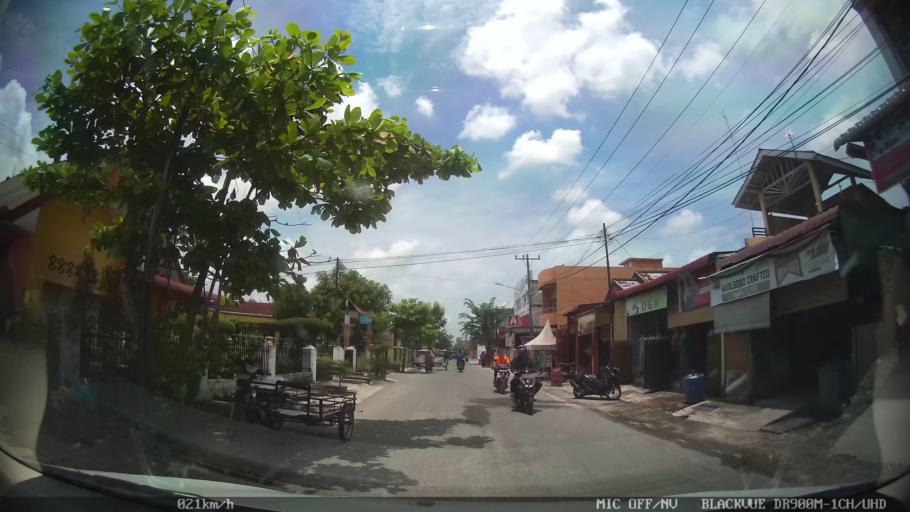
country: ID
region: North Sumatra
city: Percut
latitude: 3.5569
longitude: 98.8751
